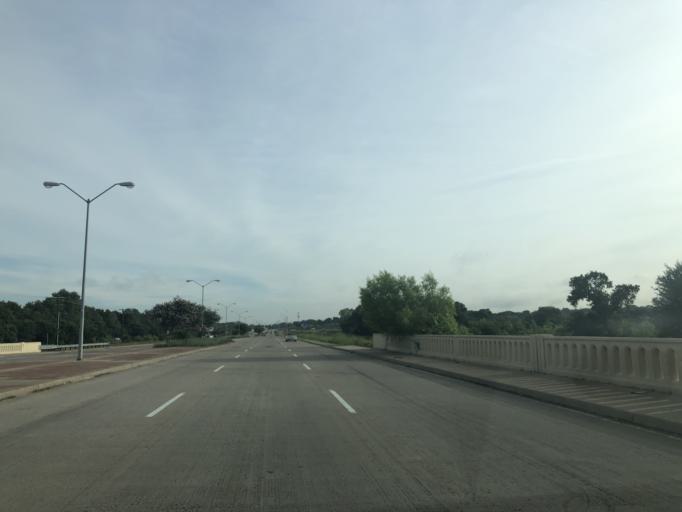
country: US
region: Texas
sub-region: Dallas County
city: Irving
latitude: 32.7957
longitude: -96.9945
